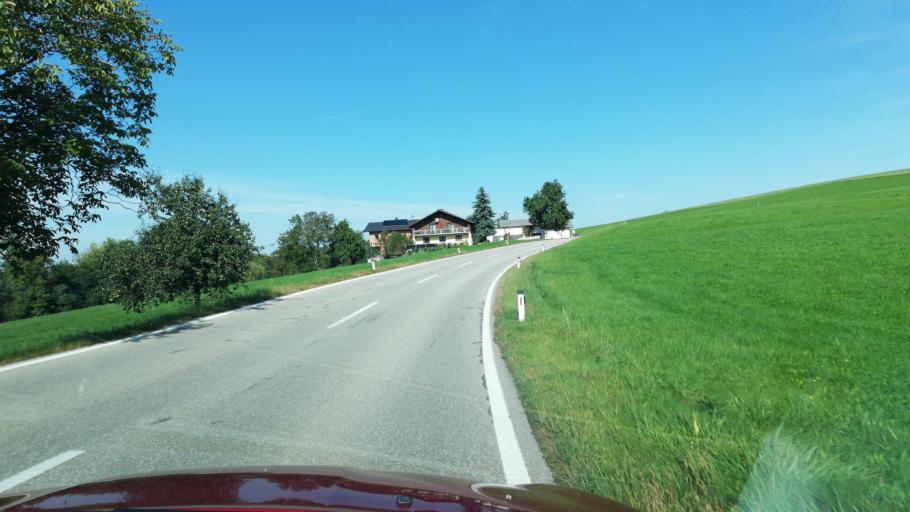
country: AT
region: Upper Austria
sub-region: Politischer Bezirk Vocklabruck
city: Zell am Pettenfirst
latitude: 48.1382
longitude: 13.5692
